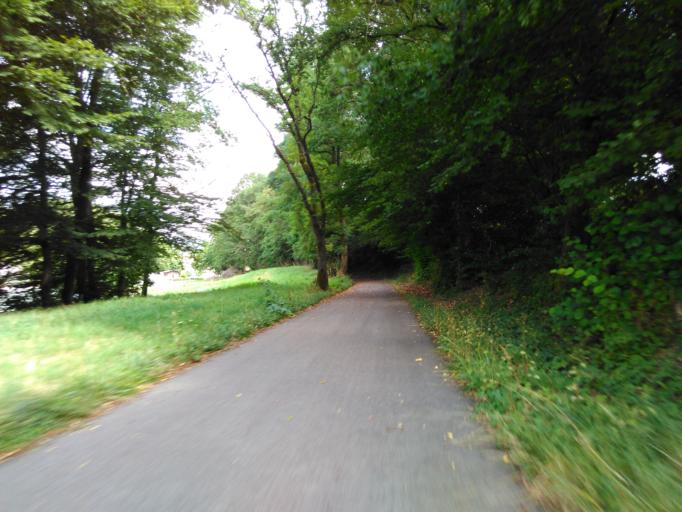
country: LU
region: Grevenmacher
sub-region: Canton d'Echternach
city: Consdorf
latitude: 49.7378
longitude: 6.3173
